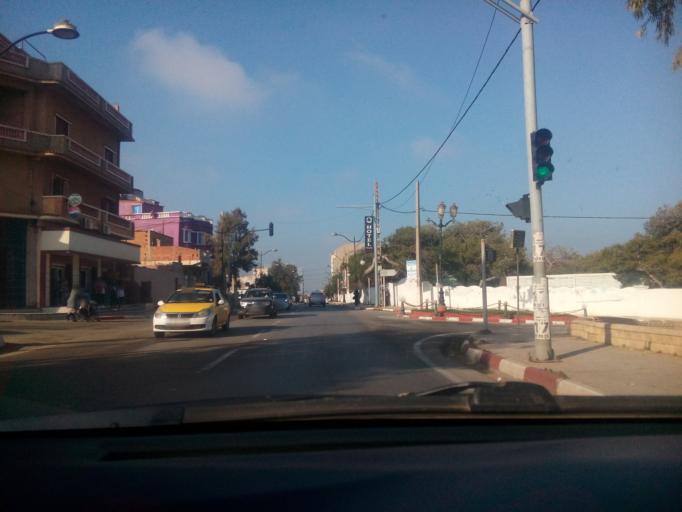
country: DZ
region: Oran
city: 'Ain el Turk
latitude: 35.7359
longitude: -0.7425
